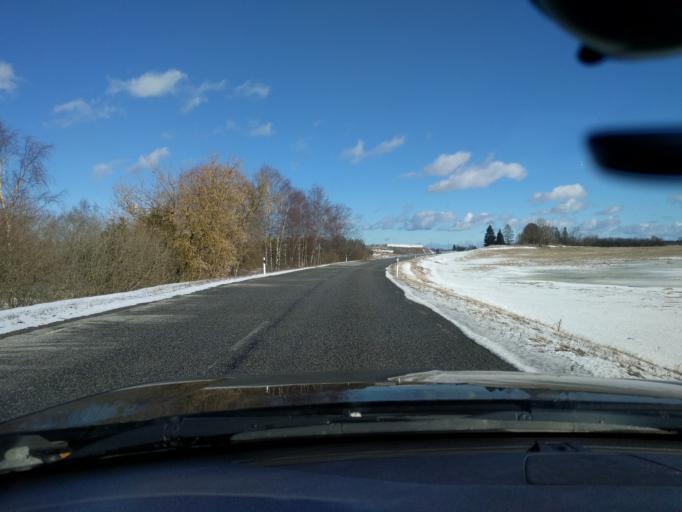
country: EE
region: Harju
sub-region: Raasiku vald
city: Raasiku
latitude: 59.3973
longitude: 25.1886
